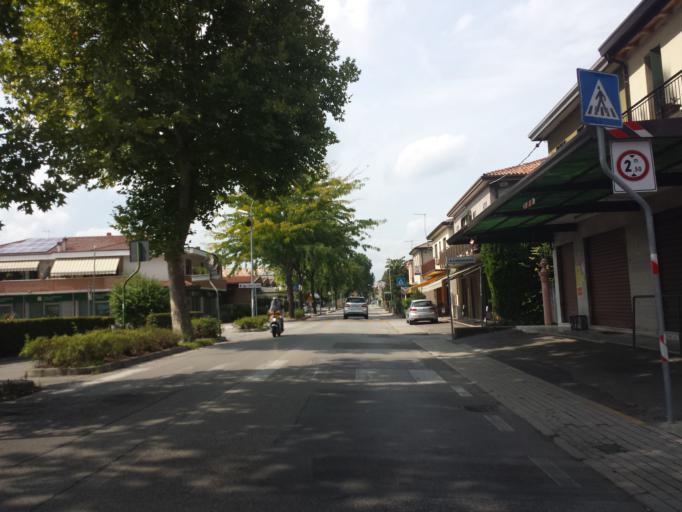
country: IT
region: Veneto
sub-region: Provincia di Padova
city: Padova
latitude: 45.4234
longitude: 11.8540
